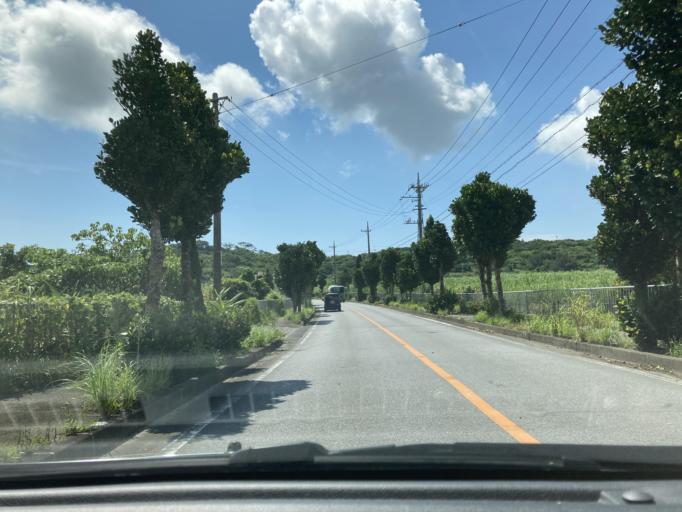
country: JP
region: Okinawa
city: Tomigusuku
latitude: 26.1556
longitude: 127.7724
